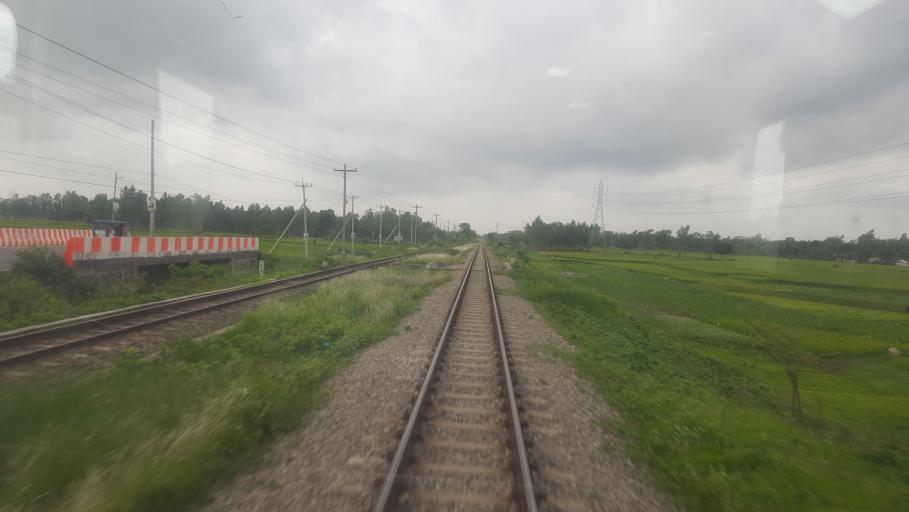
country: BD
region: Dhaka
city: Bhairab Bazar
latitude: 23.9857
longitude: 90.8521
